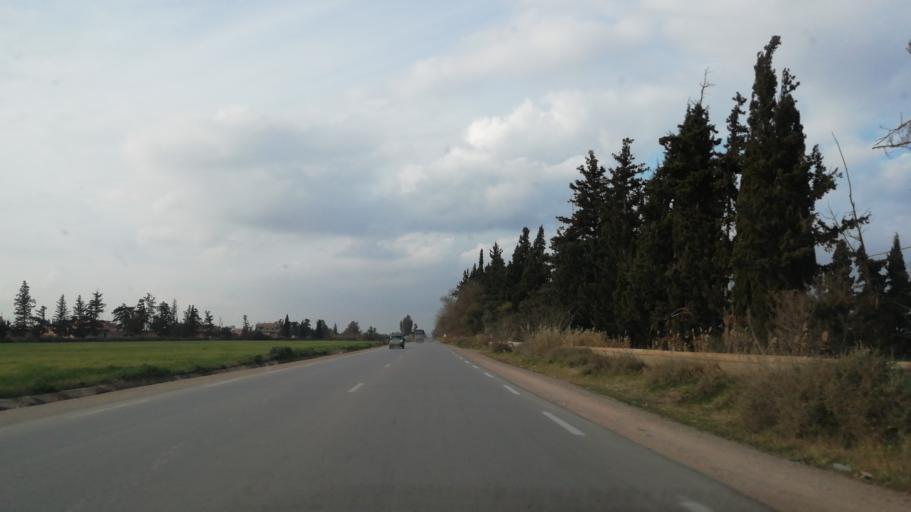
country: DZ
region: Mascara
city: Sig
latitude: 35.6781
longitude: -0.0084
